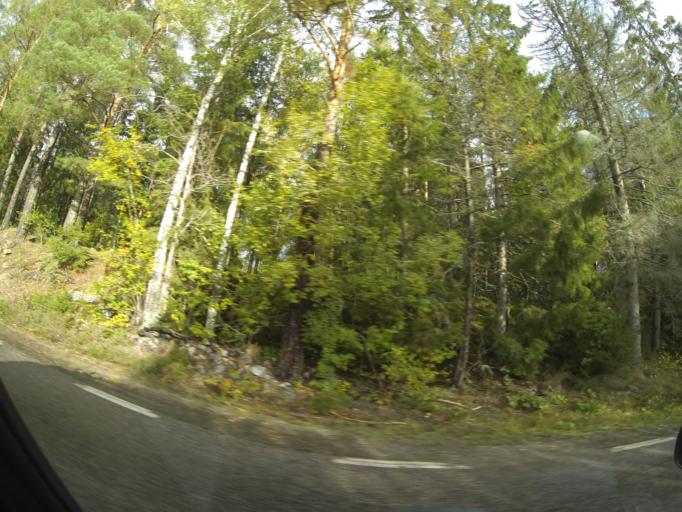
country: SE
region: Soedermanland
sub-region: Eskilstuna Kommun
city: Kvicksund
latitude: 59.3251
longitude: 16.2620
